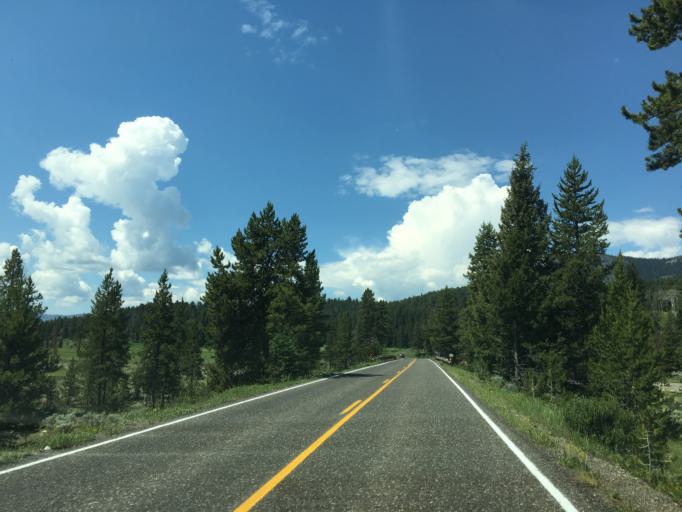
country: US
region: Montana
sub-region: Park County
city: Livingston
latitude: 44.9153
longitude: -110.1110
